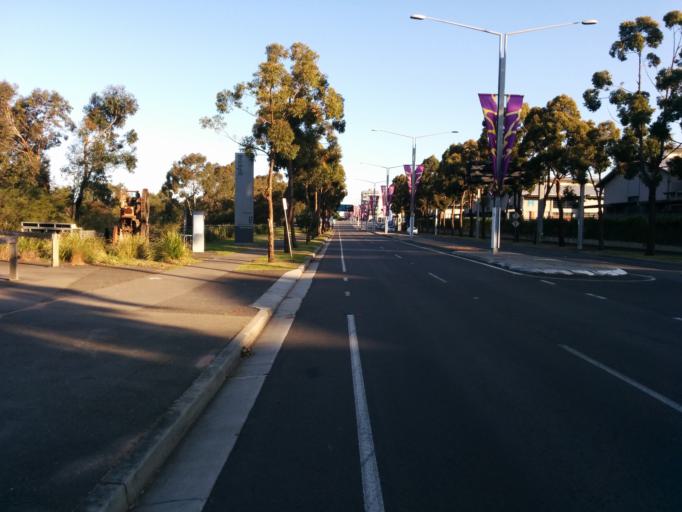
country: AU
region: New South Wales
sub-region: Canada Bay
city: Concord West
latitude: -33.8410
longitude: 151.0693
